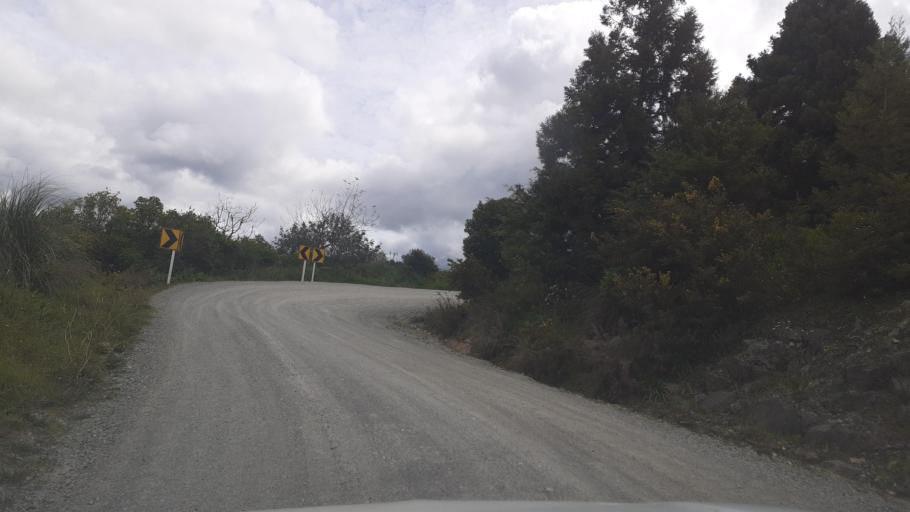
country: NZ
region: Northland
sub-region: Far North District
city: Moerewa
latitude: -35.3891
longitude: 173.9975
